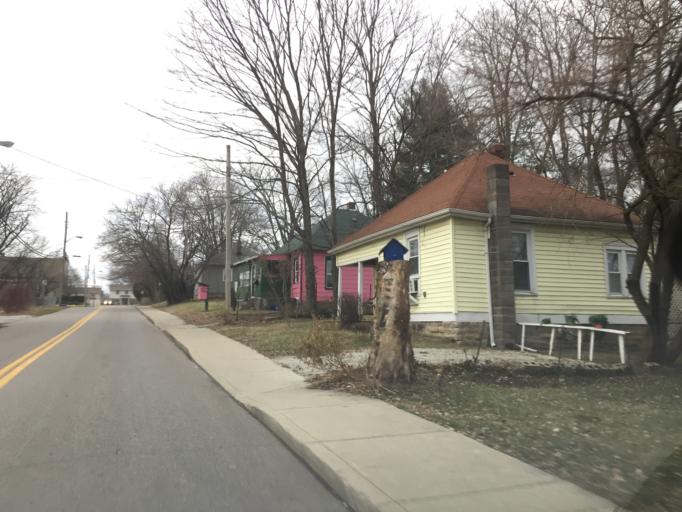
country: US
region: Indiana
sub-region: Monroe County
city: Bloomington
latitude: 39.1715
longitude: -86.5498
